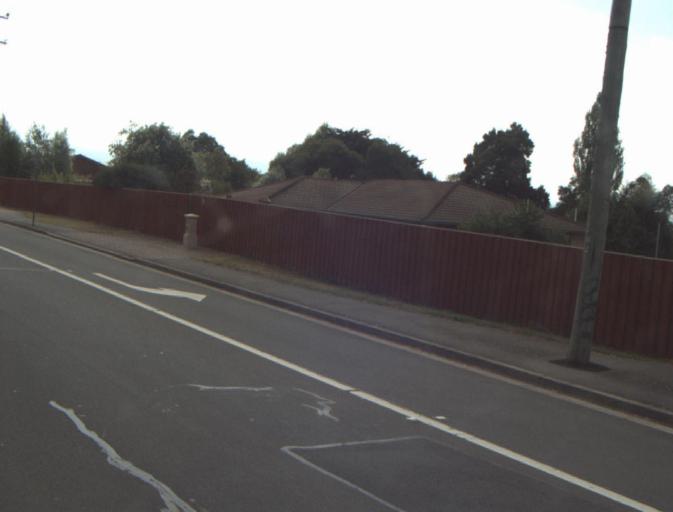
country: AU
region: Tasmania
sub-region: Launceston
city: Newstead
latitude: -41.4711
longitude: 147.1735
